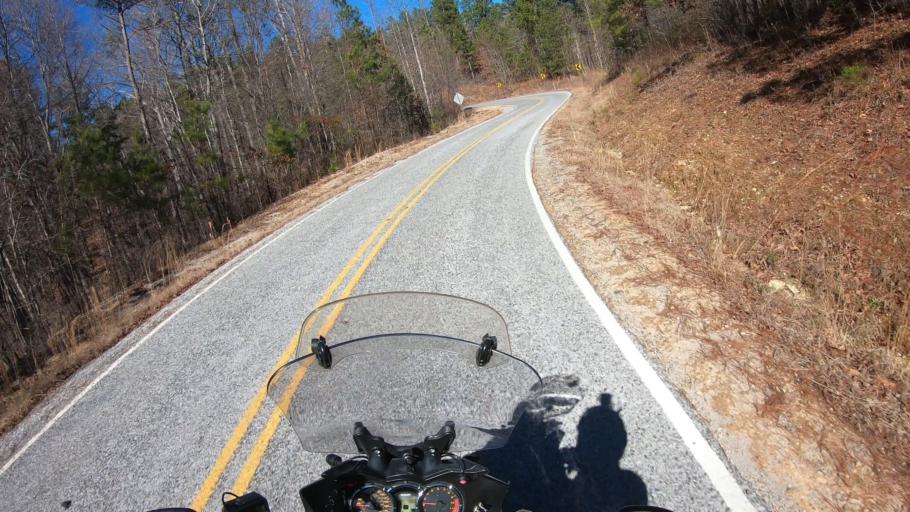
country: US
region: Alabama
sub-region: Clay County
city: Ashland
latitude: 33.4009
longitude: -85.8699
